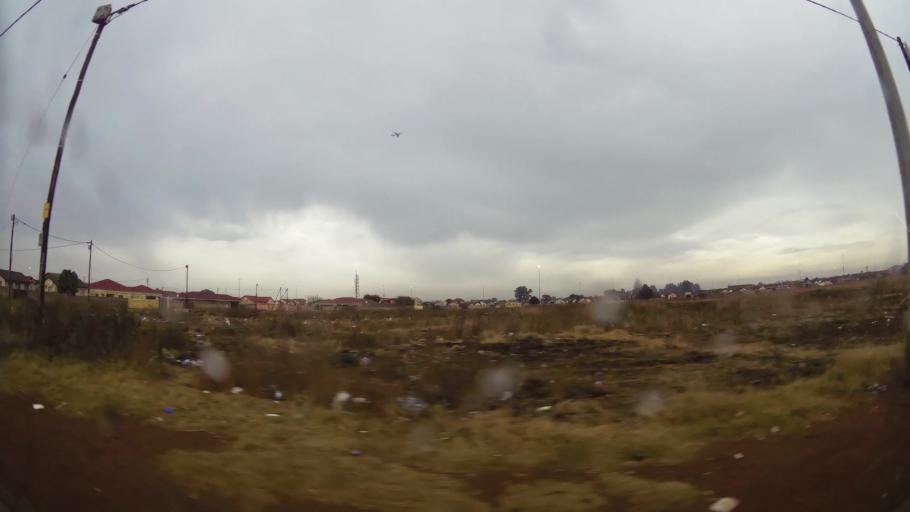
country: ZA
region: Gauteng
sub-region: Ekurhuleni Metropolitan Municipality
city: Germiston
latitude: -26.3310
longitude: 28.2000
